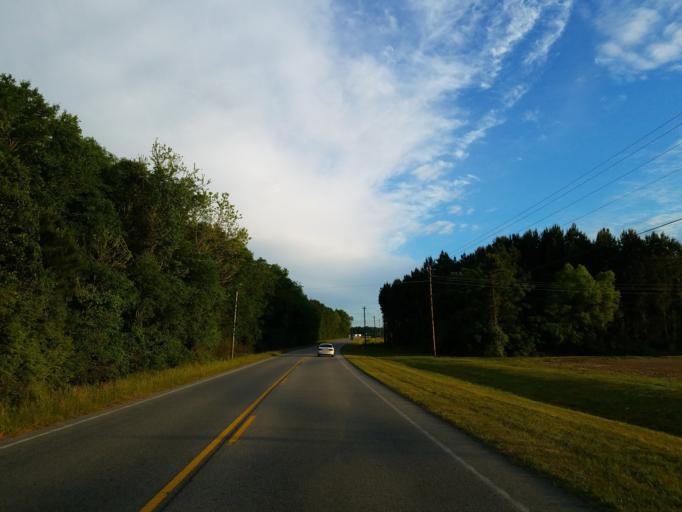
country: US
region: Georgia
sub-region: Tift County
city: Tifton
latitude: 31.4866
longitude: -83.5189
